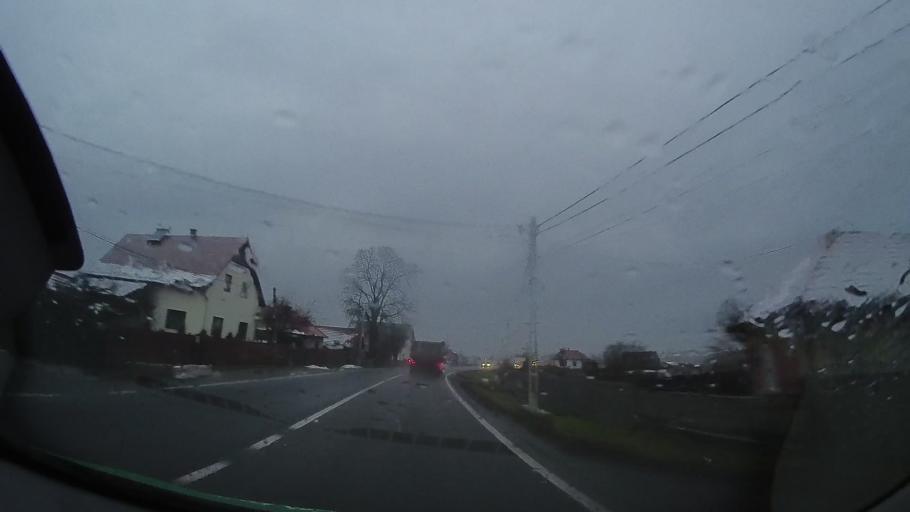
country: RO
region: Harghita
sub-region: Comuna Lazarea
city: Lazarea
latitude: 46.7575
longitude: 25.5173
